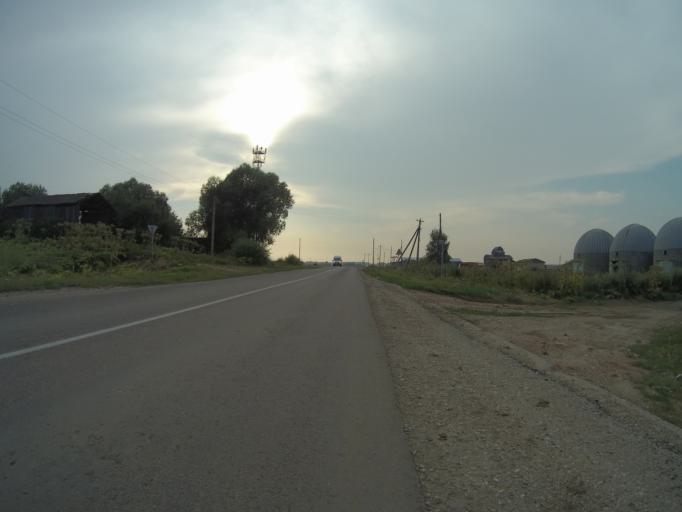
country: RU
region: Ivanovo
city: Gavrilov Posad
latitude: 56.3452
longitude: 40.1861
